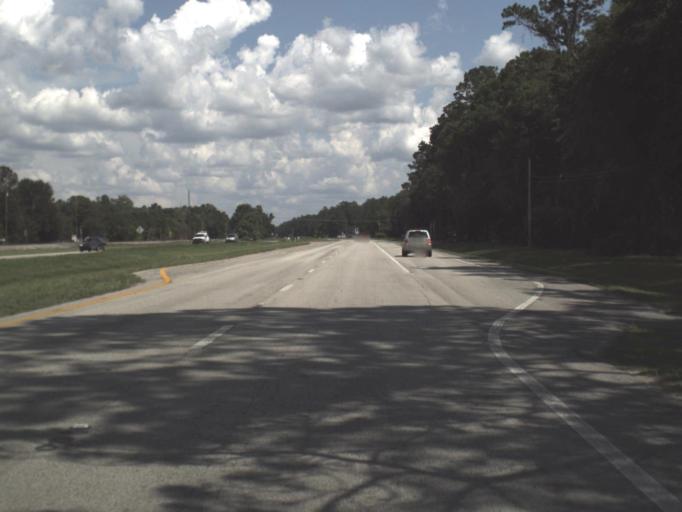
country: US
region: Florida
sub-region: Alachua County
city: Alachua
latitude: 29.7358
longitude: -82.3811
